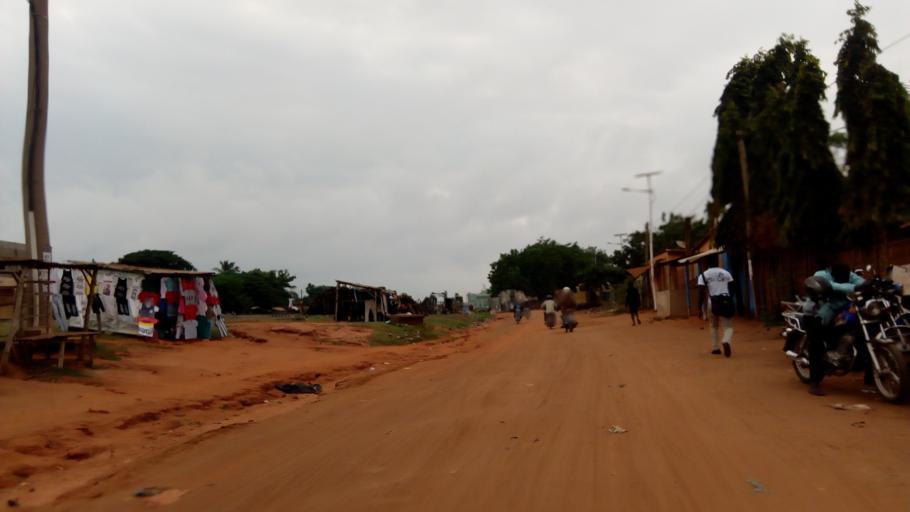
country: TG
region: Maritime
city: Lome
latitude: 6.1633
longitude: 1.2062
